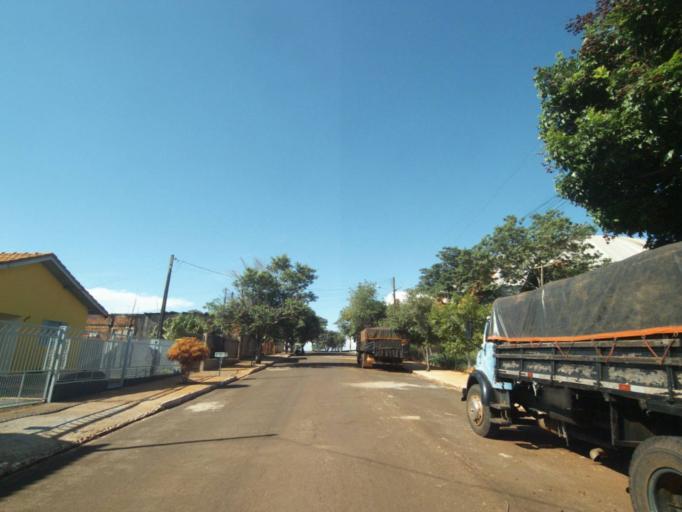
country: BR
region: Parana
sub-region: Sertanopolis
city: Sertanopolis
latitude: -23.0351
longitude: -50.8140
